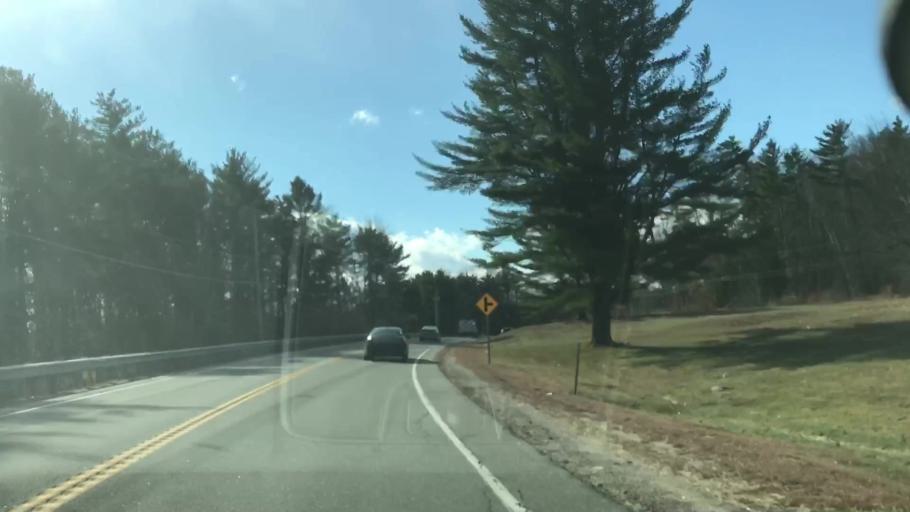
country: US
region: New Hampshire
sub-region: Carroll County
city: Wolfeboro
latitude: 43.6120
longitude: -71.1771
